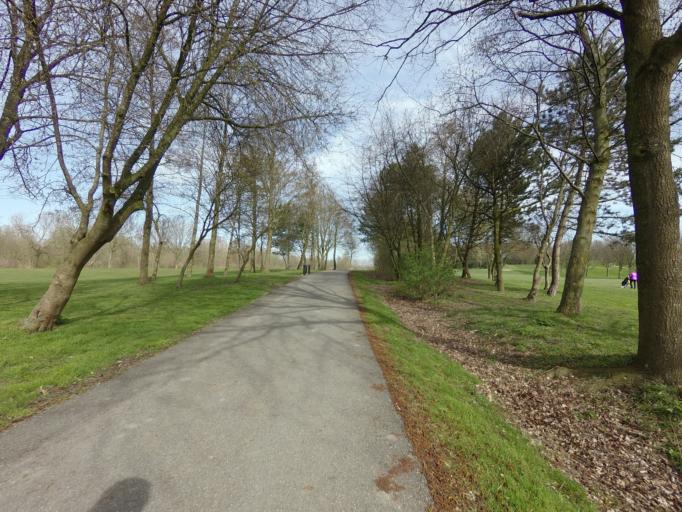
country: NL
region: South Holland
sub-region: Gemeente Alphen aan den Rijn
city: Alphen aan den Rijn
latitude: 52.1407
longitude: 4.6944
